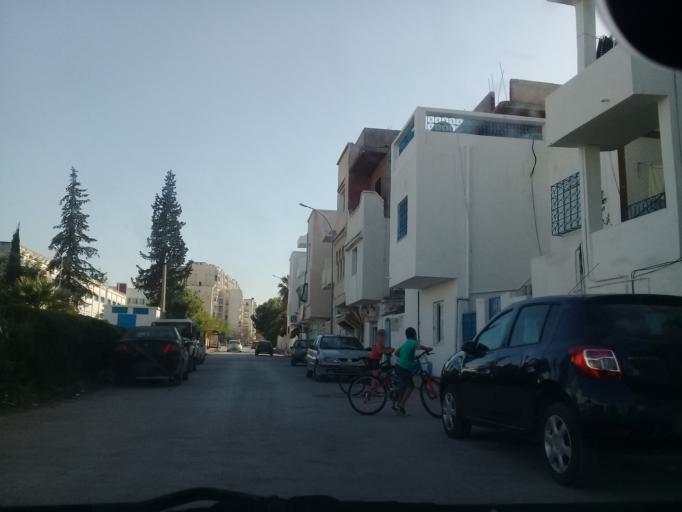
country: TN
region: Ariana
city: Ariana
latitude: 36.8340
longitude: 10.1912
